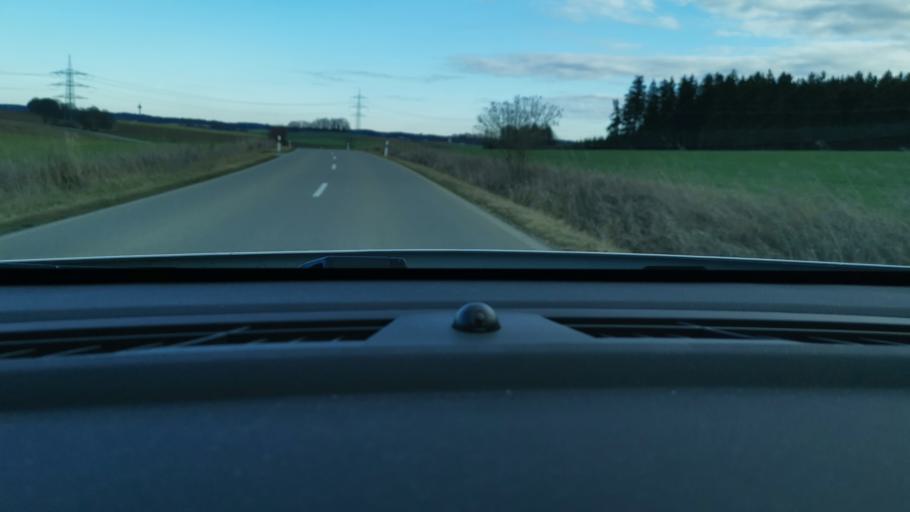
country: DE
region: Bavaria
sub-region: Swabia
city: Aindling
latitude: 48.4888
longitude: 10.9644
